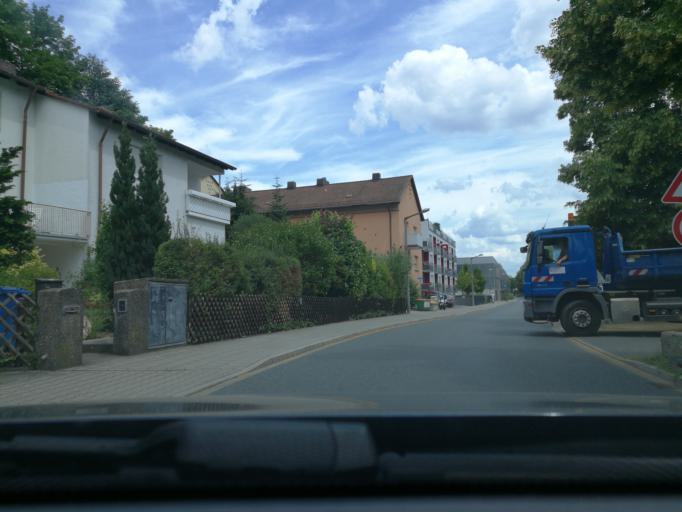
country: DE
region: Bavaria
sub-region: Regierungsbezirk Mittelfranken
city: Furth
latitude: 49.4757
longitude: 10.9748
